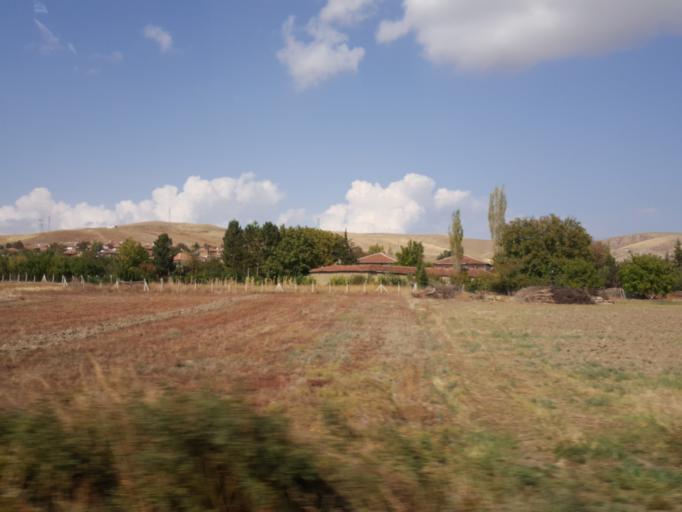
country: TR
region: Corum
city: Bogazkale
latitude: 40.1527
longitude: 34.5962
